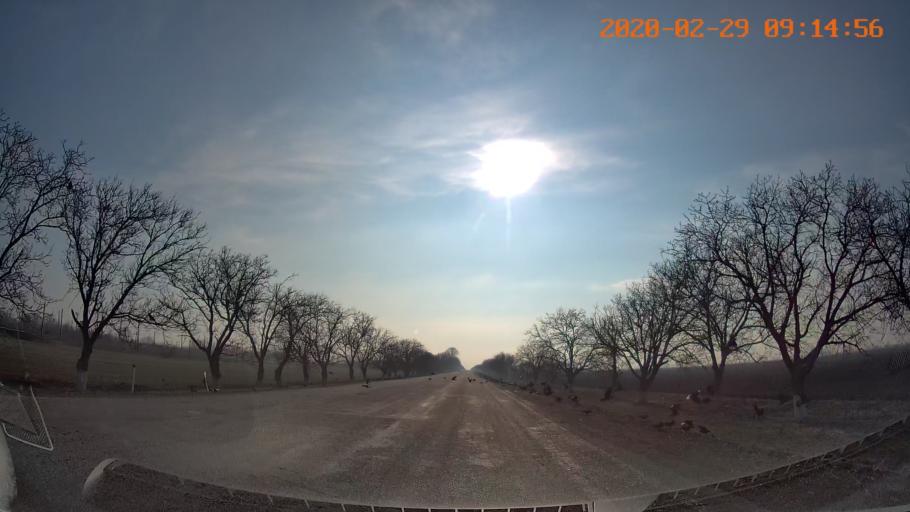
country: MD
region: Telenesti
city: Pervomaisc
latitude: 46.8045
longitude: 29.8611
